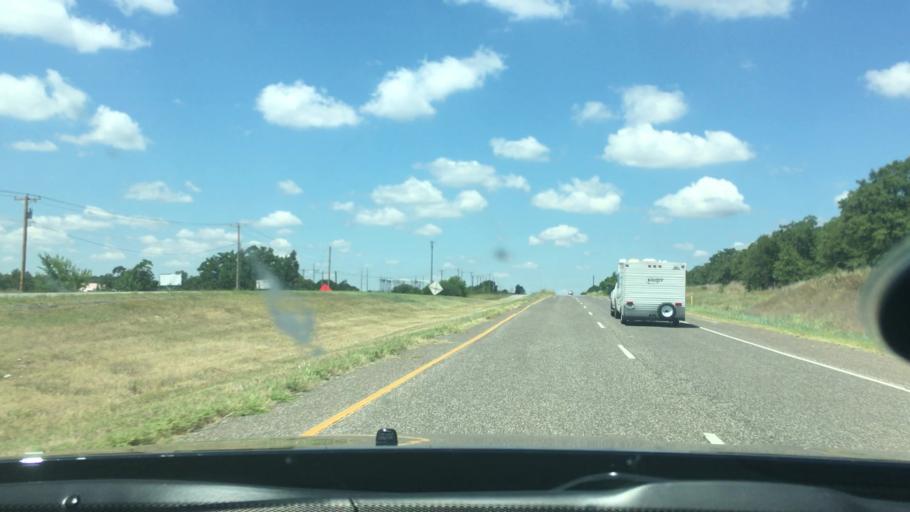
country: US
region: Oklahoma
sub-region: Carter County
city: Lone Grove
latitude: 34.1730
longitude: -97.3265
